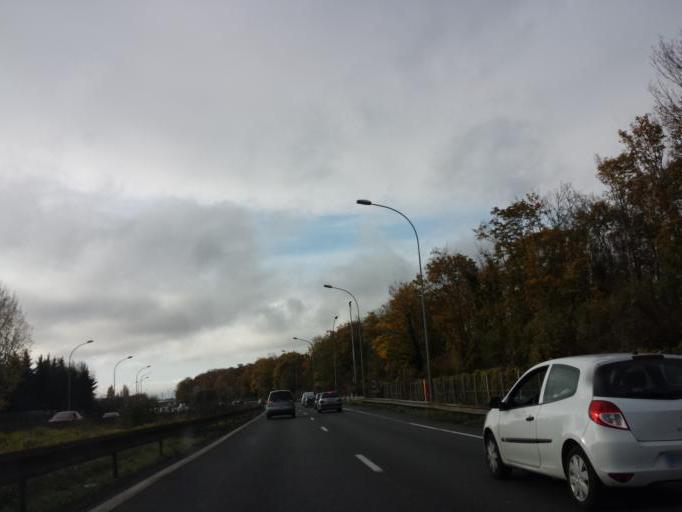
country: FR
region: Ile-de-France
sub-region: Departement du Val-d'Oise
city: Bezons
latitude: 48.9232
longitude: 2.2285
